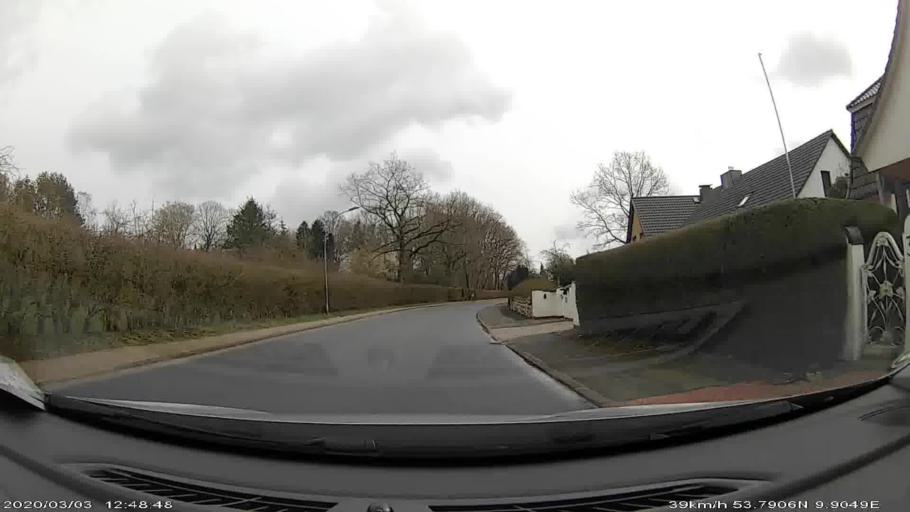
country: DE
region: Schleswig-Holstein
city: Alveslohe
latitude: 53.7903
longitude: 9.9065
